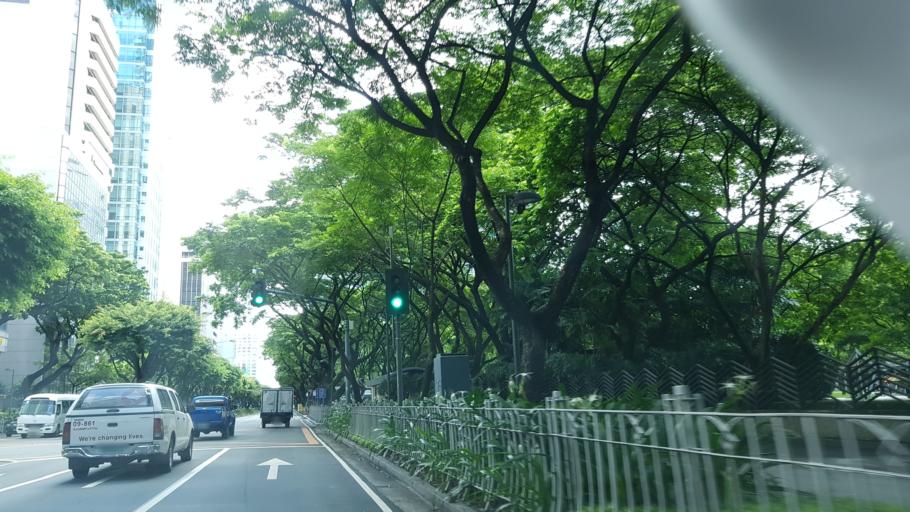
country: PH
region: Metro Manila
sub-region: Makati City
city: Makati City
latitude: 14.5570
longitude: 121.0224
